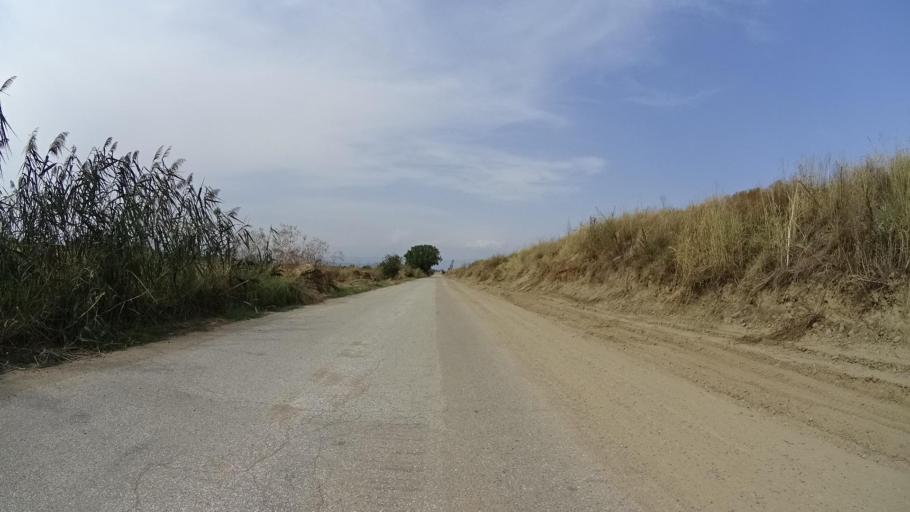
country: BG
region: Plovdiv
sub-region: Obshtina Kaloyanovo
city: Kaloyanovo
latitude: 42.3087
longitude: 24.7996
